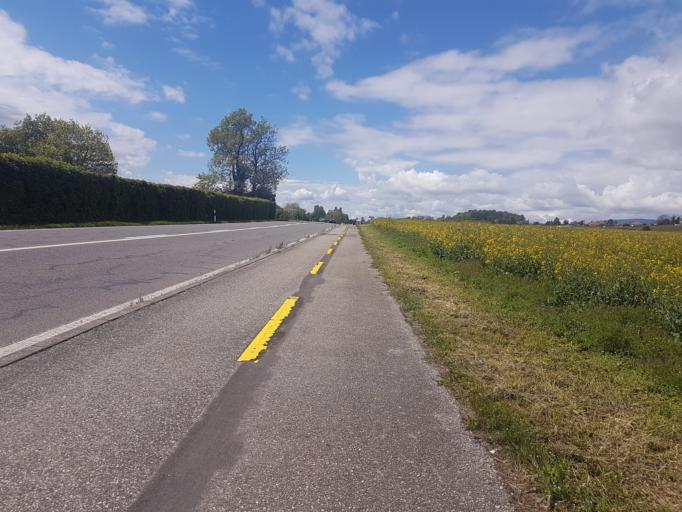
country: CH
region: Vaud
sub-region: Nyon District
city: Rolle
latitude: 46.4373
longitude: 6.3104
